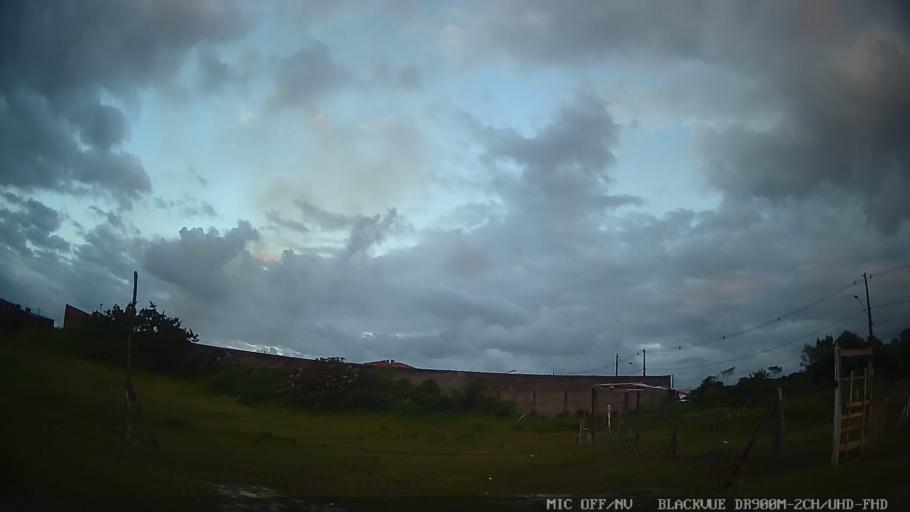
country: BR
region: Sao Paulo
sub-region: Itanhaem
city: Itanhaem
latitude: -24.1847
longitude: -46.8366
